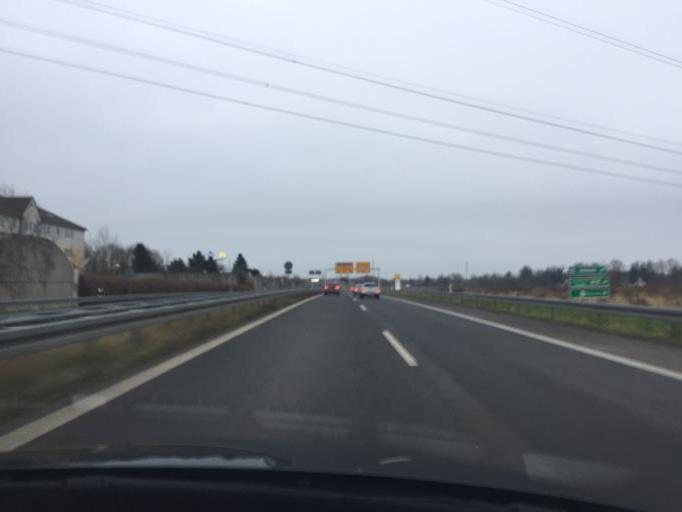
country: DE
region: Berlin
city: Lichtenrade
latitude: 52.3611
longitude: 13.4284
